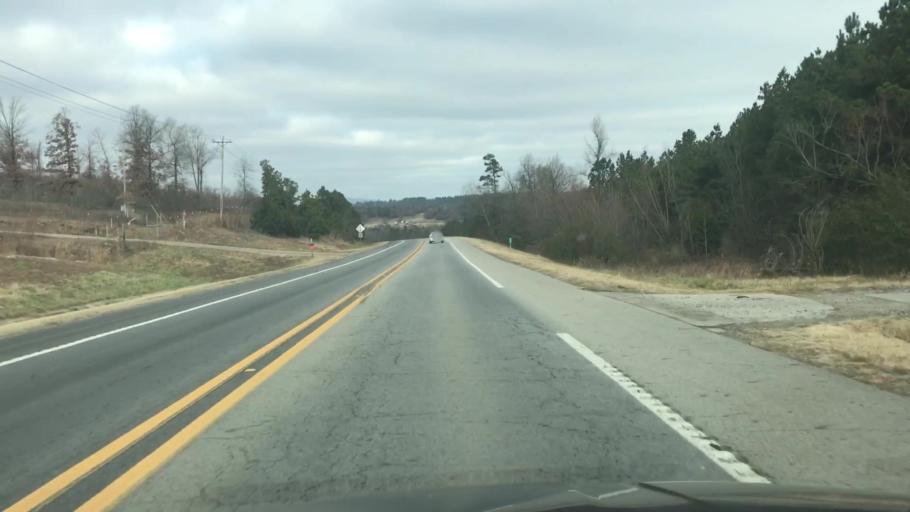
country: US
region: Arkansas
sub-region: Scott County
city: Waldron
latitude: 34.8416
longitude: -94.0538
